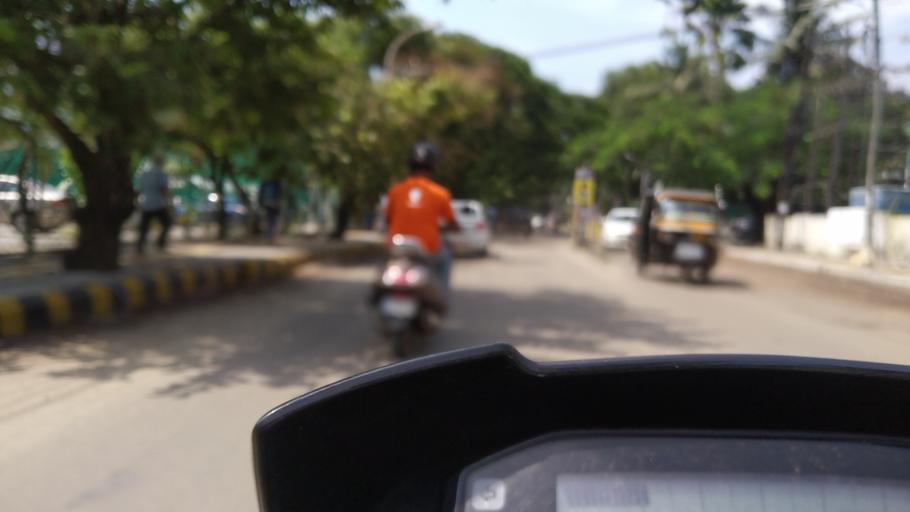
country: IN
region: Kerala
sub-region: Ernakulam
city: Cochin
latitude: 9.9692
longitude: 76.2982
